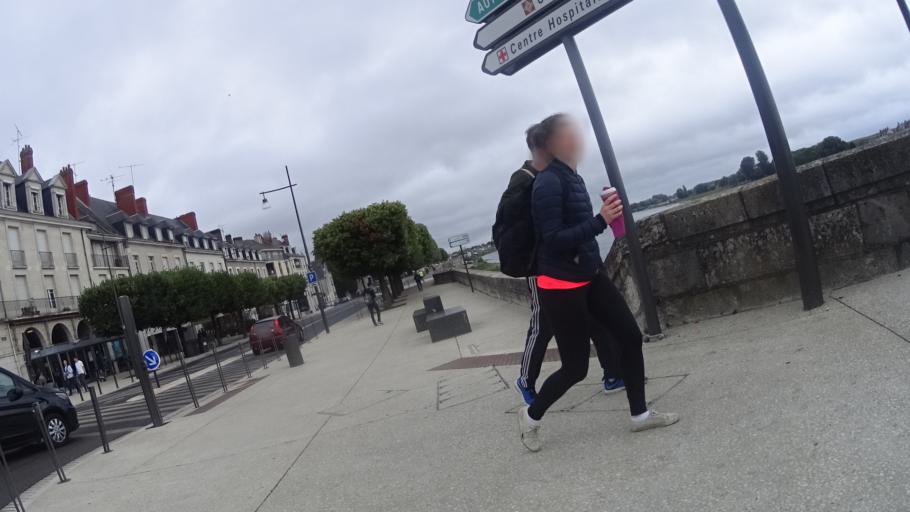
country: FR
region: Centre
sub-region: Departement du Loir-et-Cher
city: Blois
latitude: 47.5860
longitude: 1.3363
